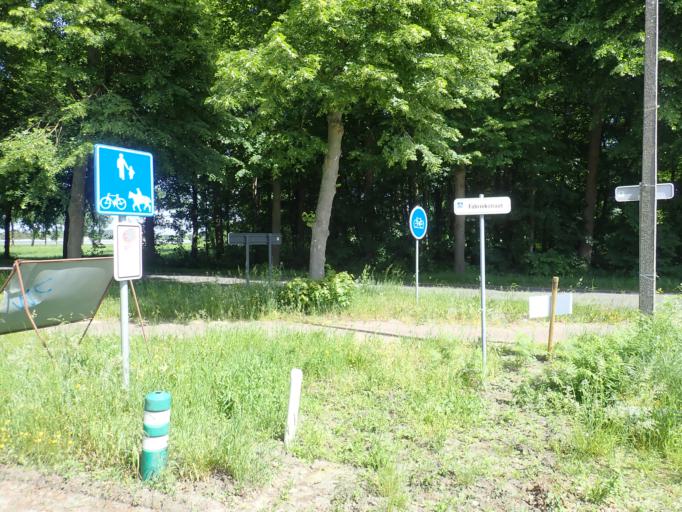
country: BE
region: Flanders
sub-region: Provincie Antwerpen
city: Hulshout
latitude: 51.0949
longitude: 4.8169
